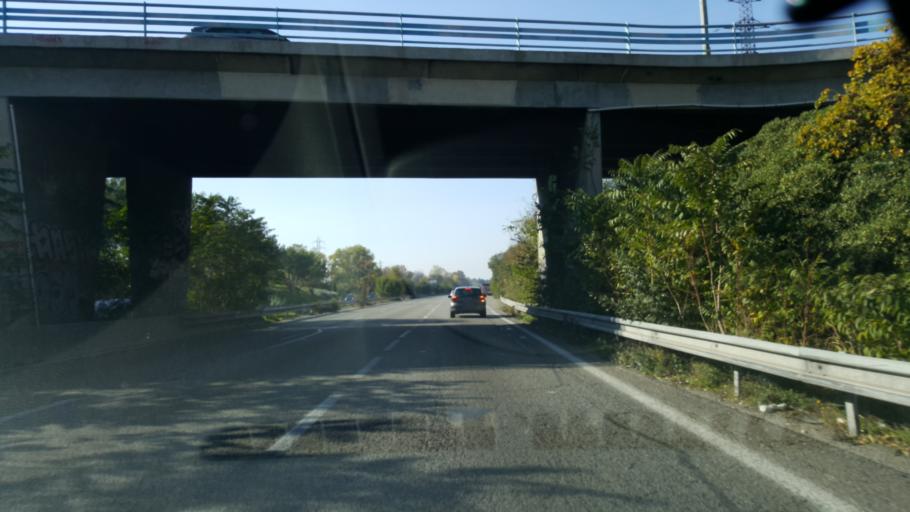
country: FR
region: Provence-Alpes-Cote d'Azur
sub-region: Departement des Bouches-du-Rhone
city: La Penne-sur-Huveaune
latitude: 43.2855
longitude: 5.5146
